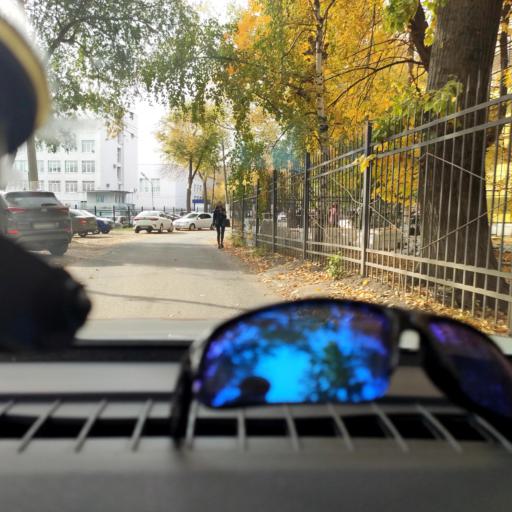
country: RU
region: Samara
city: Samara
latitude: 53.2181
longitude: 50.2123
